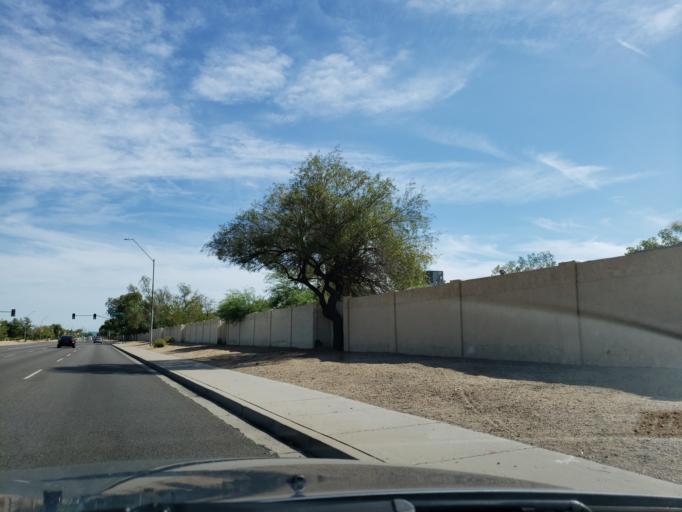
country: US
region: Arizona
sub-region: Maricopa County
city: Glendale
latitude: 33.6024
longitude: -112.1512
